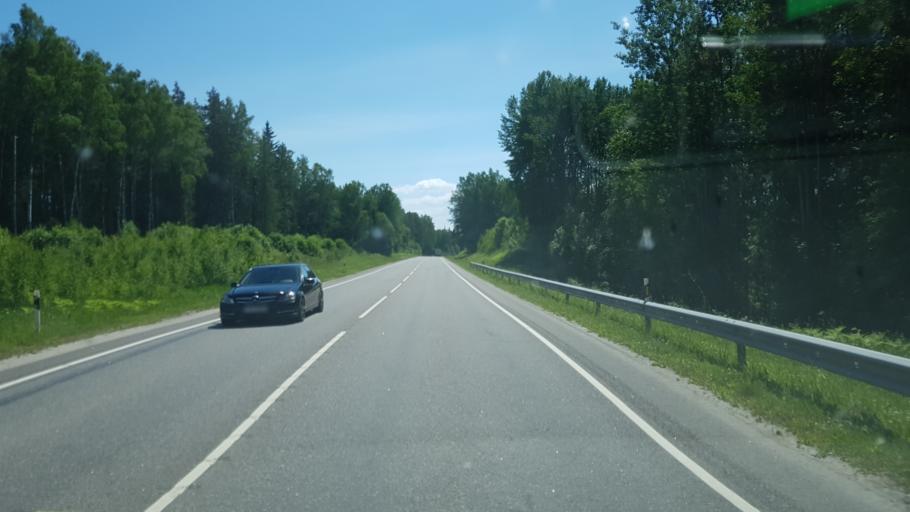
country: EE
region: Tartu
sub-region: UElenurme vald
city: Ulenurme
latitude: 58.1076
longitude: 26.7384
